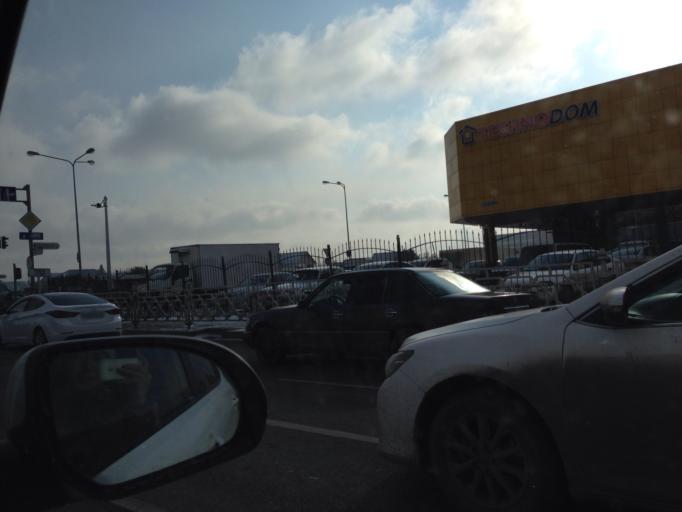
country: KZ
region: Astana Qalasy
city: Astana
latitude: 51.1784
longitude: 71.4359
